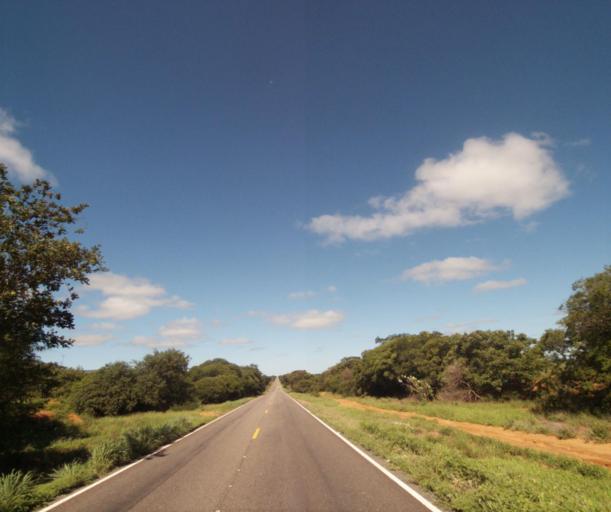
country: BR
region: Bahia
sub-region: Palmas De Monte Alto
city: Palmas de Monte Alto
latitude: -14.2382
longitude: -43.0205
